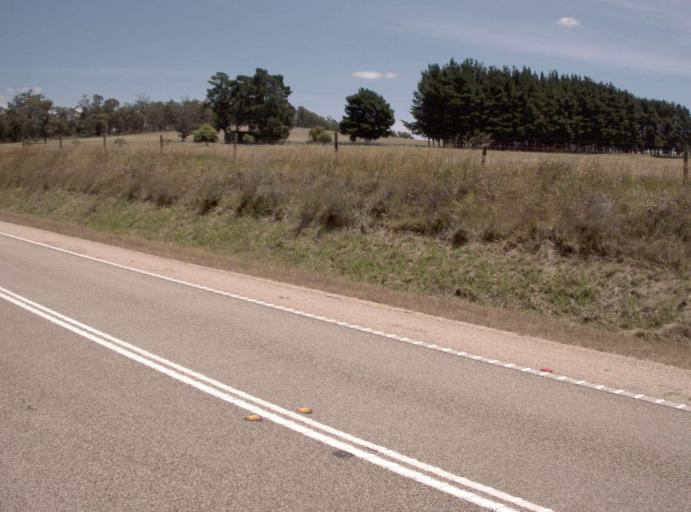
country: AU
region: Victoria
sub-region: East Gippsland
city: Bairnsdale
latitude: -37.7682
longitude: 147.6950
